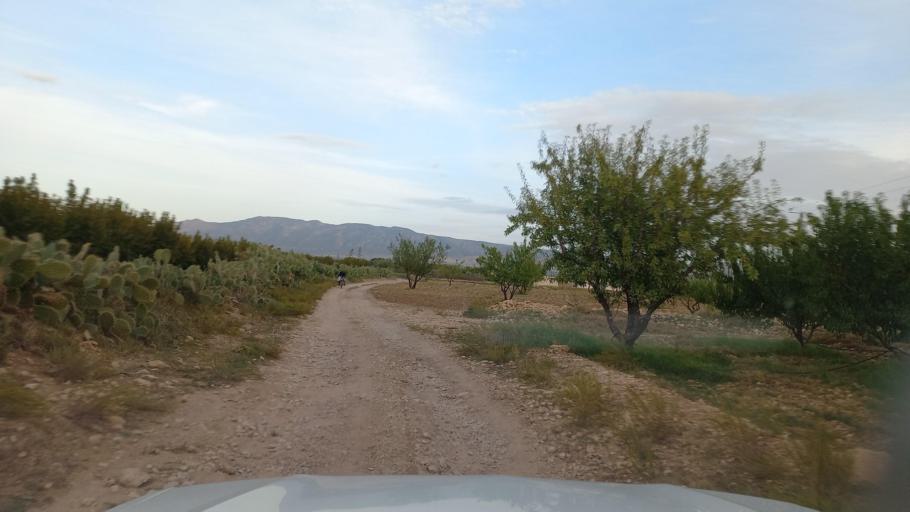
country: TN
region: Al Qasrayn
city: Sbiba
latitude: 35.4229
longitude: 9.1004
